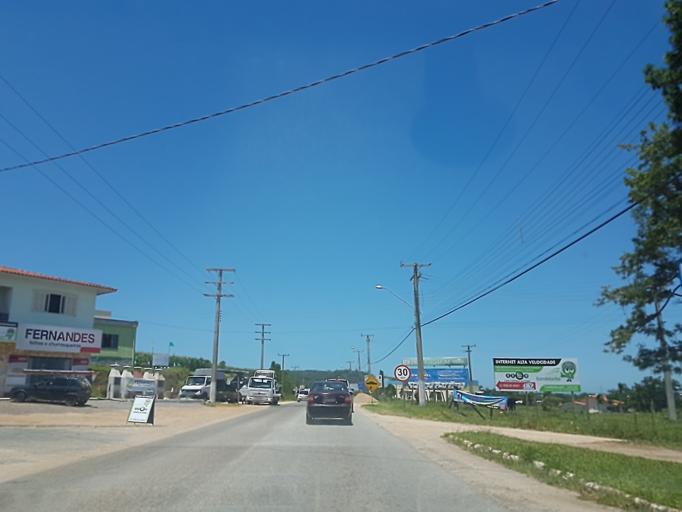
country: BR
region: Santa Catarina
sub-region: Jaguaruna
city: Jaguaruna
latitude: -28.6010
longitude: -49.0480
